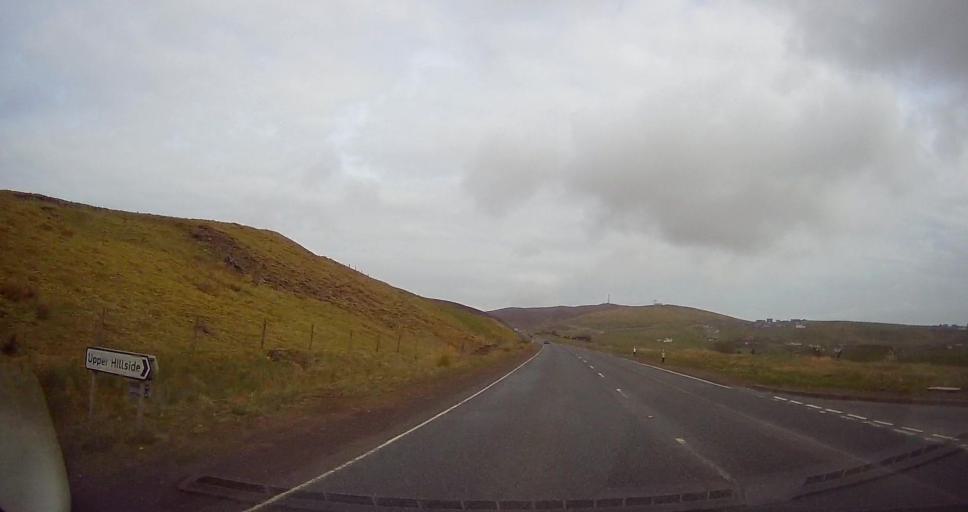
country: GB
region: Scotland
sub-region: Shetland Islands
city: Lerwick
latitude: 60.1279
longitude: -1.2162
